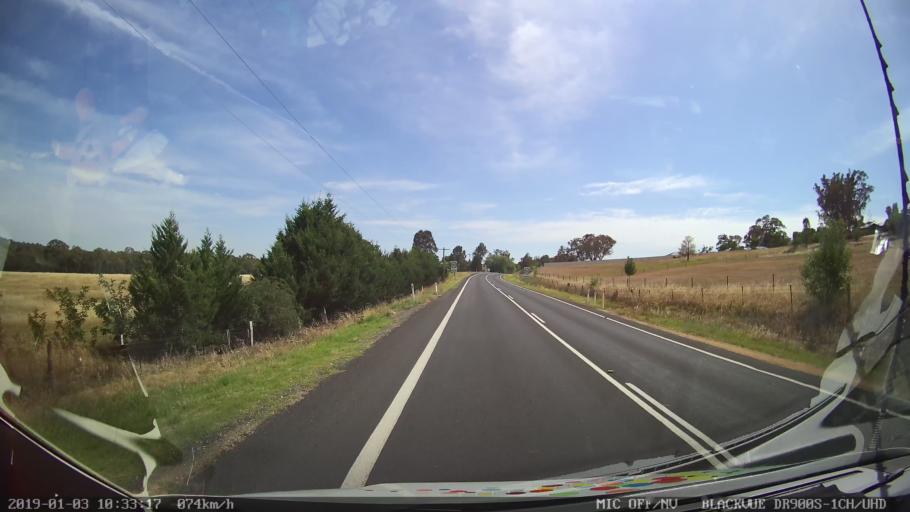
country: AU
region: New South Wales
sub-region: Young
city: Young
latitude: -34.3298
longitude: 148.2866
